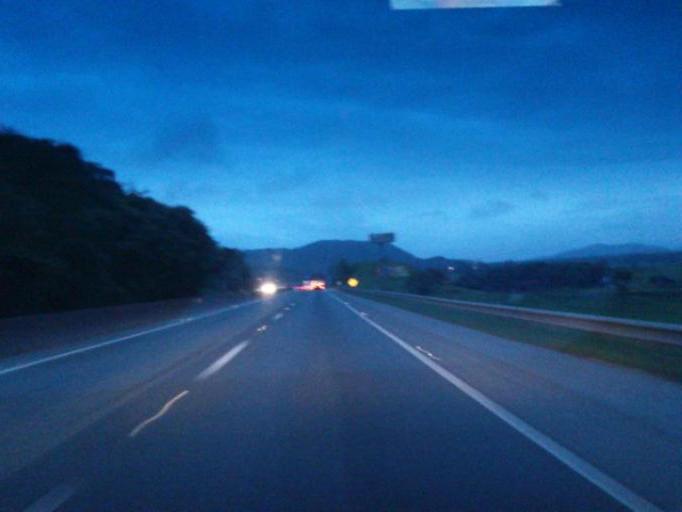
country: BR
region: Santa Catarina
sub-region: Penha
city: Penha
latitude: -26.8248
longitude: -48.6891
